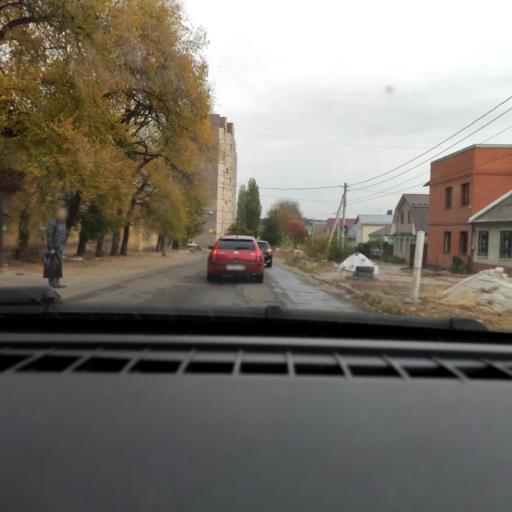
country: RU
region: Voronezj
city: Voronezh
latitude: 51.6750
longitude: 39.2617
